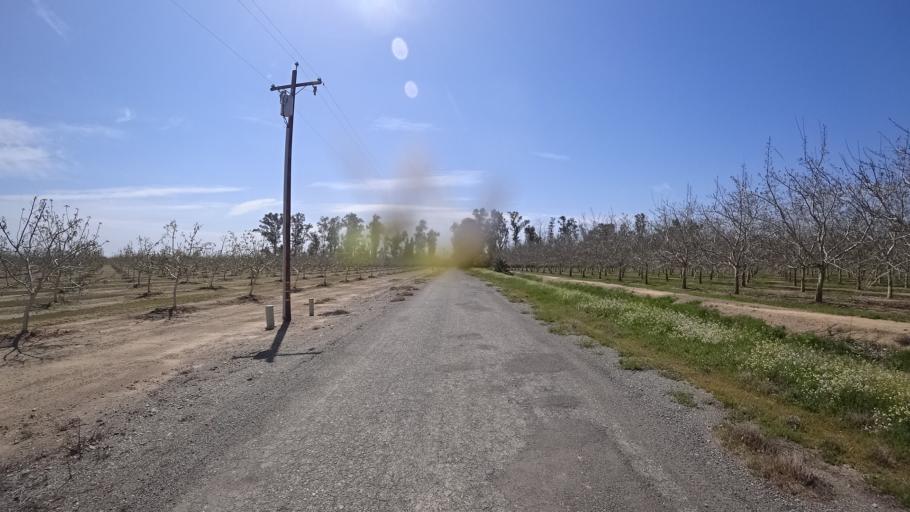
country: US
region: California
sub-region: Glenn County
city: Hamilton City
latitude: 39.6362
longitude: -122.0743
